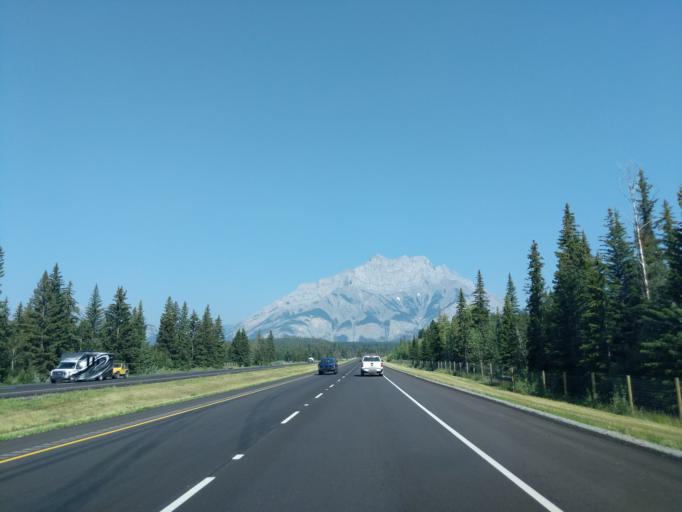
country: CA
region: Alberta
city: Banff
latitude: 51.1778
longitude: -115.4758
